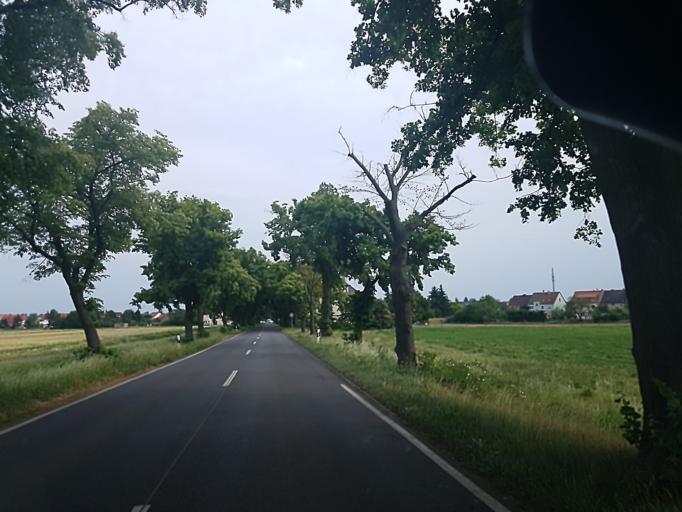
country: DE
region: Saxony-Anhalt
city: Wittenburg
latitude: 51.8820
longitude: 12.6293
